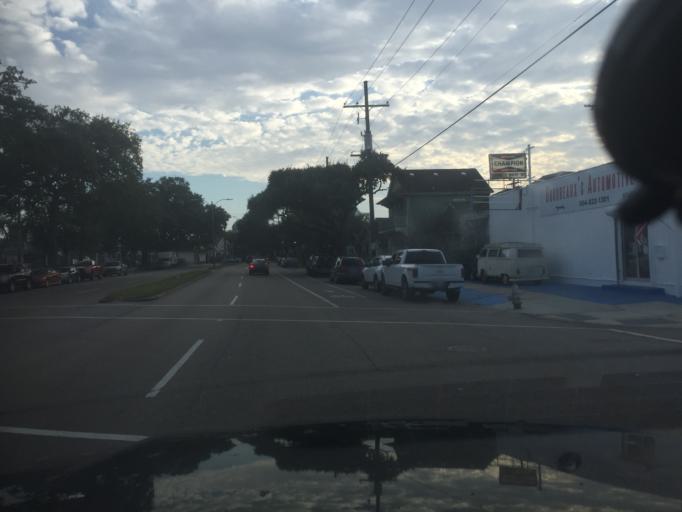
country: US
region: Louisiana
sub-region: Orleans Parish
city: New Orleans
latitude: 29.9809
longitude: -90.0775
